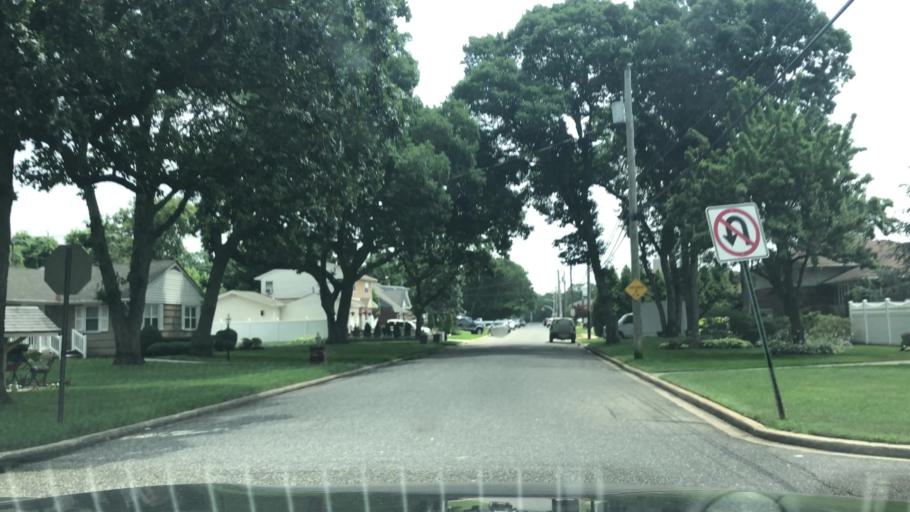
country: US
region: New York
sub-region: Nassau County
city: North Massapequa
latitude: 40.7047
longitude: -73.4651
